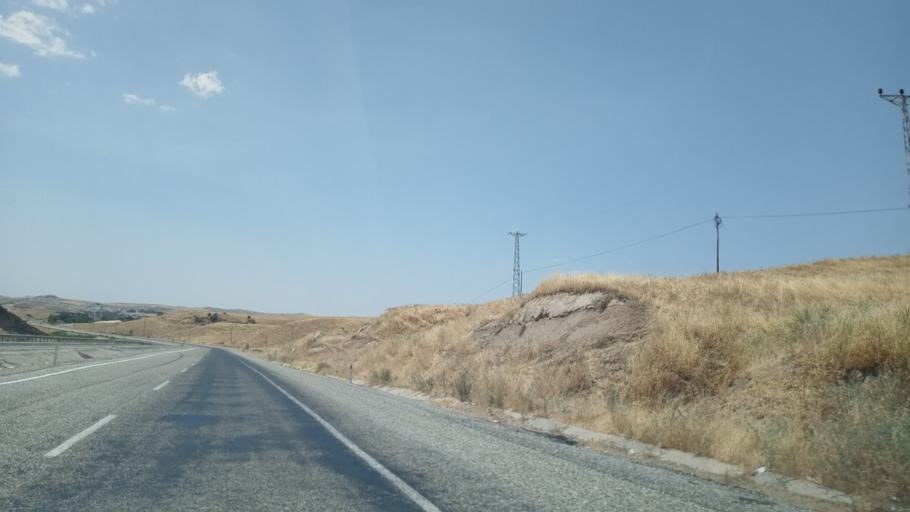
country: TR
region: Batman
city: Bekirhan
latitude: 38.1562
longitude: 41.3252
